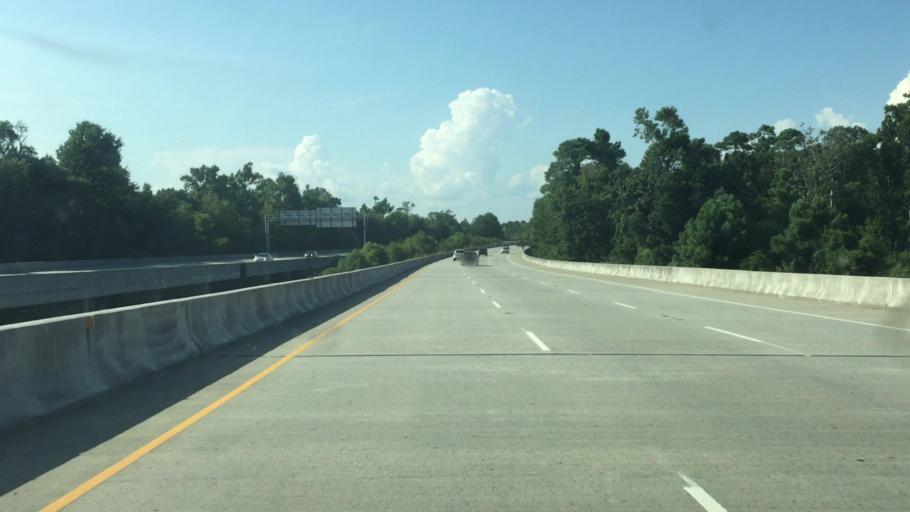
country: US
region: South Carolina
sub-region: Horry County
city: North Myrtle Beach
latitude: 33.7939
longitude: -78.7783
